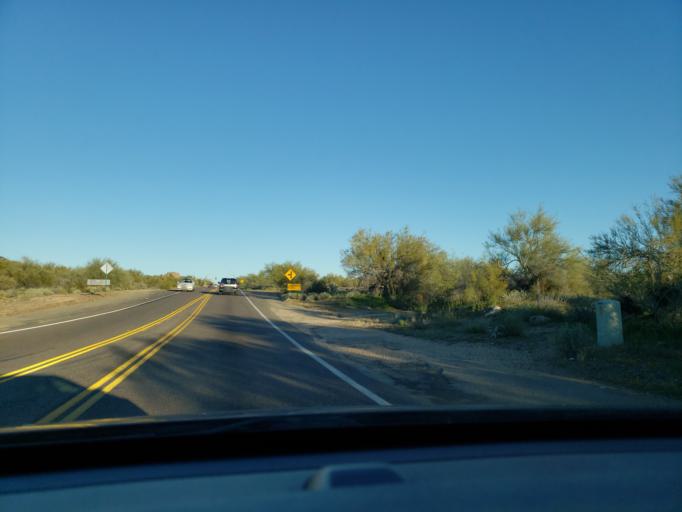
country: US
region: Arizona
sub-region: Maricopa County
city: Cave Creek
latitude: 33.7991
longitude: -111.9565
